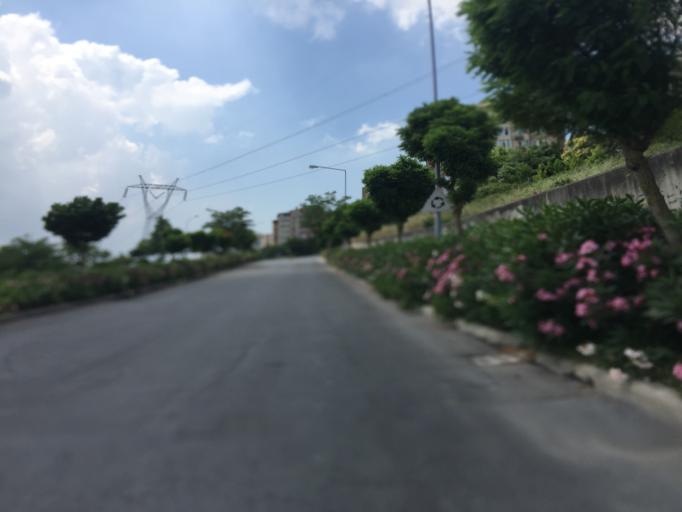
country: TR
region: Istanbul
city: Esenyurt
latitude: 41.0764
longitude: 28.6699
